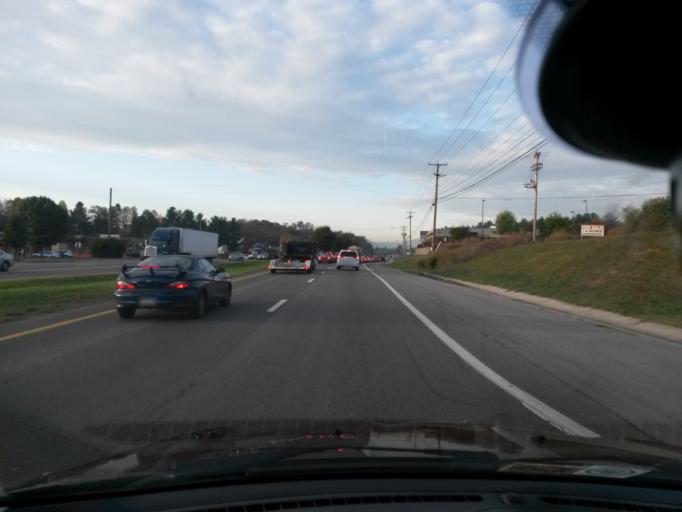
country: US
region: Virginia
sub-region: Roanoke County
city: Vinton
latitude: 37.3091
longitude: -79.8872
